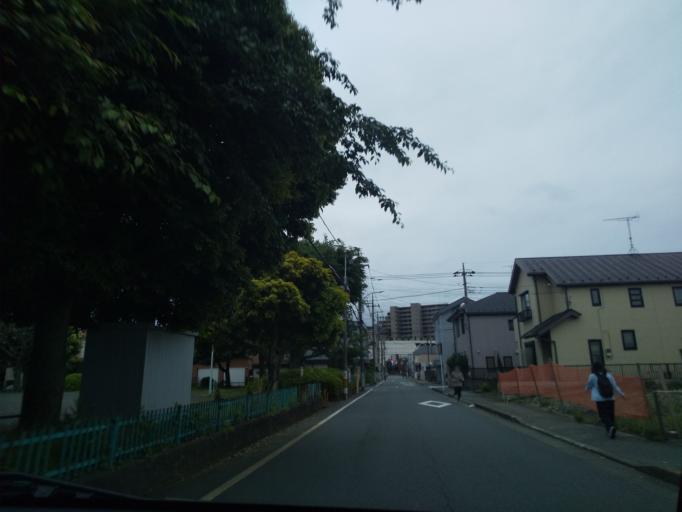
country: JP
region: Tokyo
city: Hino
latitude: 35.6639
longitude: 139.3758
